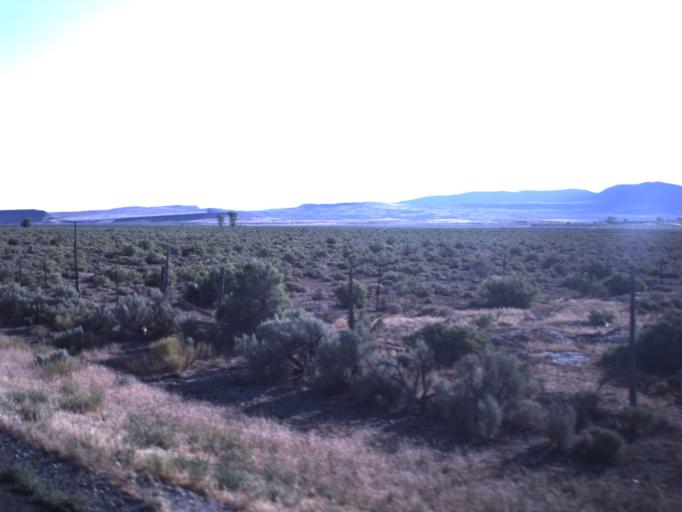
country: US
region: Utah
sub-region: Iron County
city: Enoch
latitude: 37.8038
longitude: -113.0505
